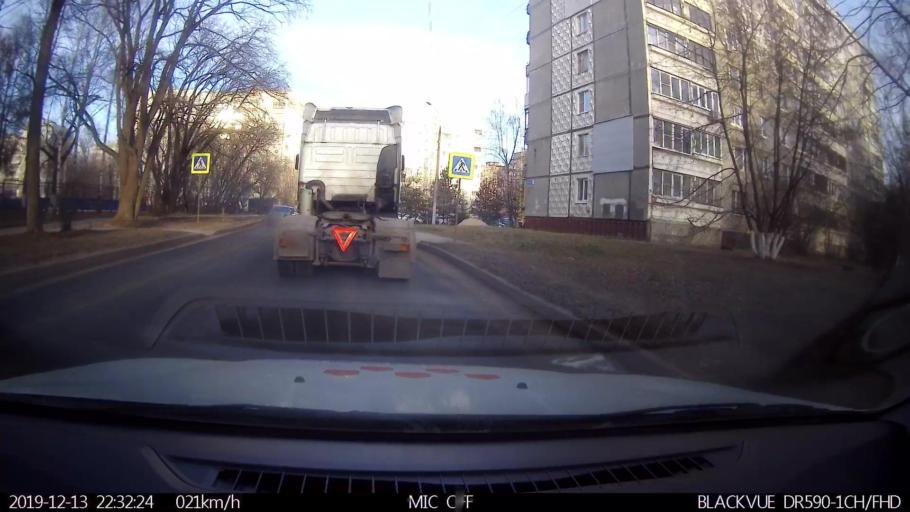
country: RU
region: Nizjnij Novgorod
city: Nizhniy Novgorod
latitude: 56.2844
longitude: 43.9505
